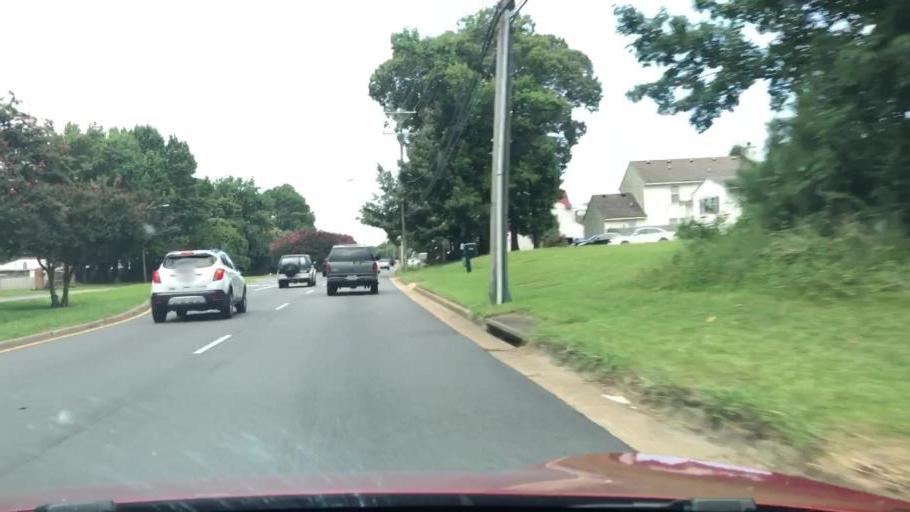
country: US
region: Virginia
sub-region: City of Norfolk
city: Norfolk
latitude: 36.8889
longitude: -76.1374
